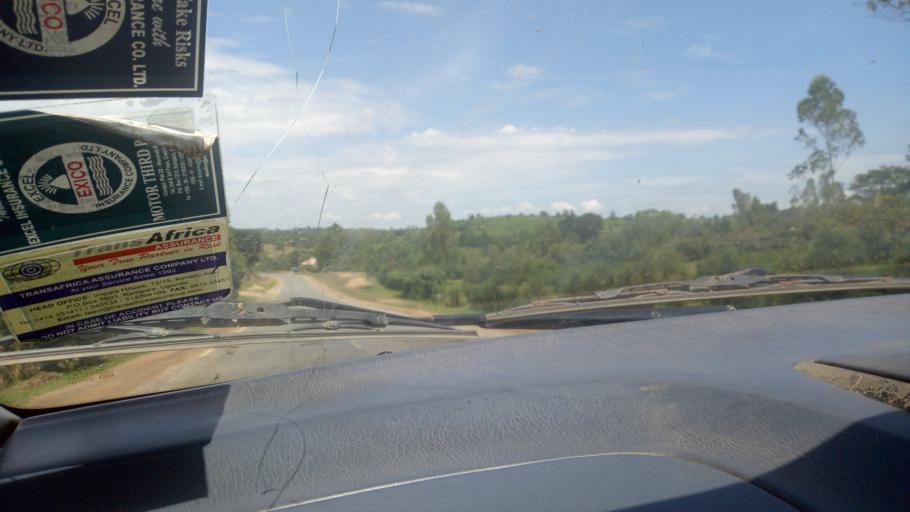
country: UG
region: Western Region
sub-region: Buhweju District
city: Buhweju
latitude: -0.2646
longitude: 30.5599
